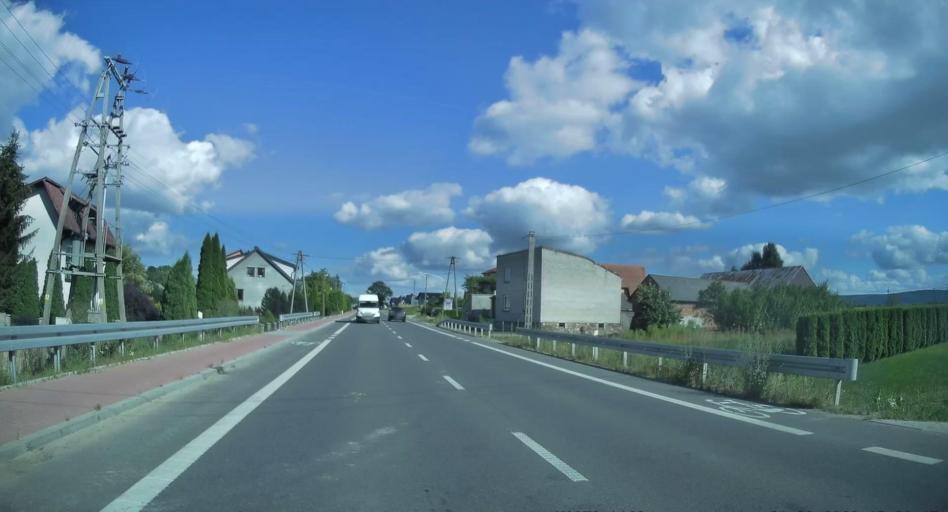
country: PL
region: Swietokrzyskie
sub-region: Powiat kielecki
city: Bodzentyn
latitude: 50.9326
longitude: 20.9699
